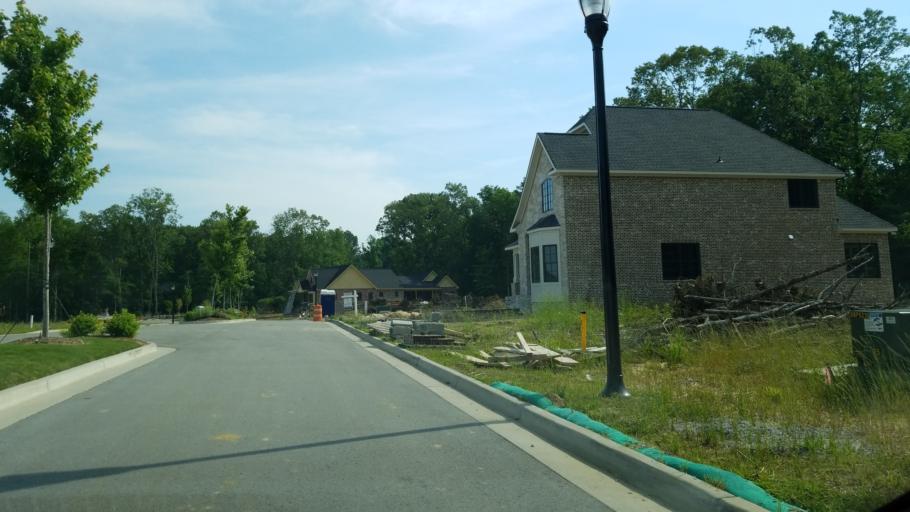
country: US
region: Tennessee
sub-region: Hamilton County
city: Collegedale
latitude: 35.0852
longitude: -85.0534
